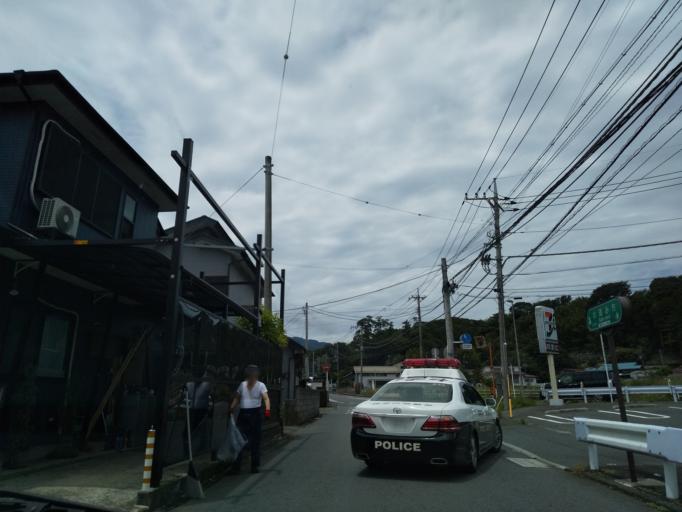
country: JP
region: Kanagawa
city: Zama
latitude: 35.5284
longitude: 139.3096
